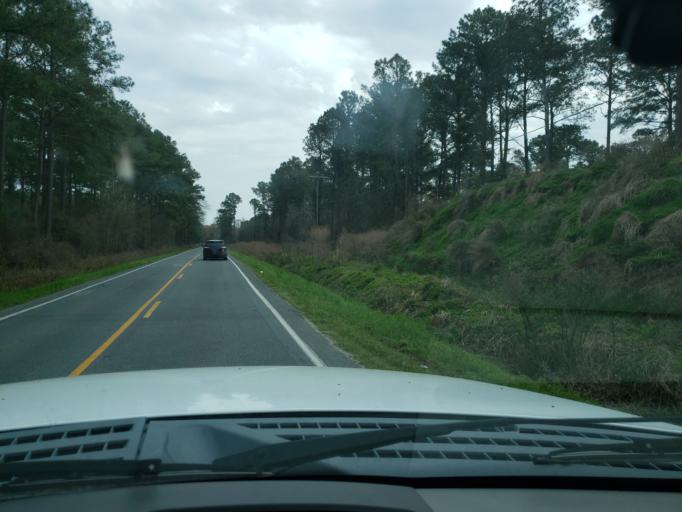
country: US
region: North Carolina
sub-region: Duplin County
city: Wallace
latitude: 34.7947
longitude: -77.8609
